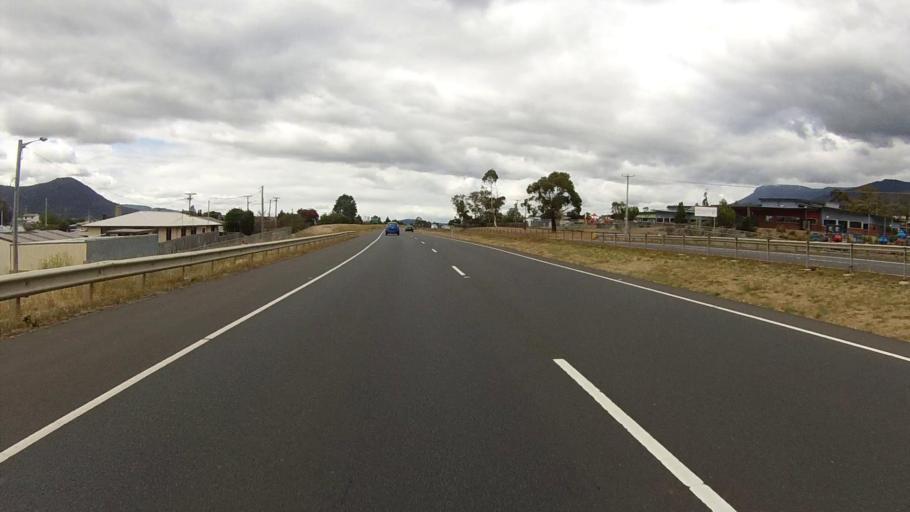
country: AU
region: Tasmania
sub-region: Glenorchy
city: Claremont
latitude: -42.7833
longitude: 147.2402
